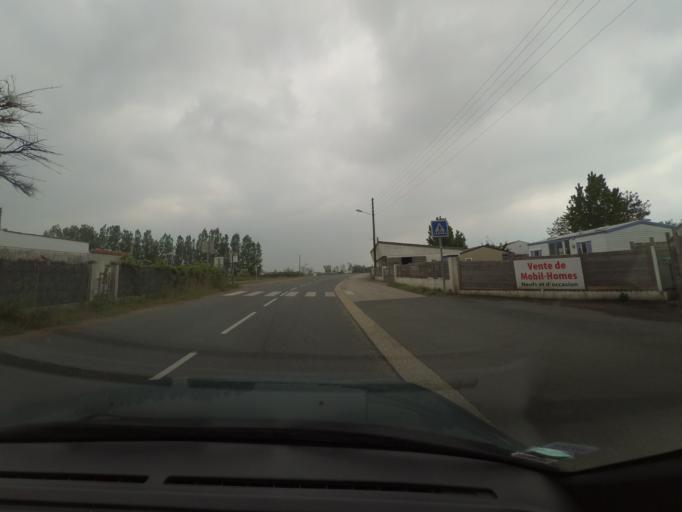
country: FR
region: Pays de la Loire
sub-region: Departement de la Vendee
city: Angles
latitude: 46.3435
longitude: -1.3441
